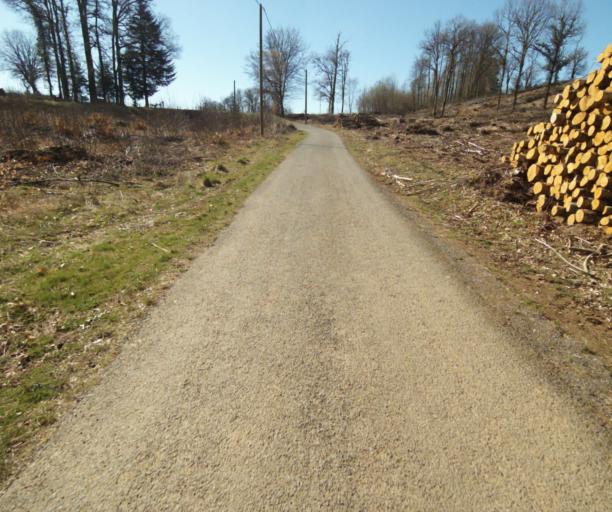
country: FR
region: Limousin
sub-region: Departement de la Correze
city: Seilhac
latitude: 45.3951
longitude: 1.7337
